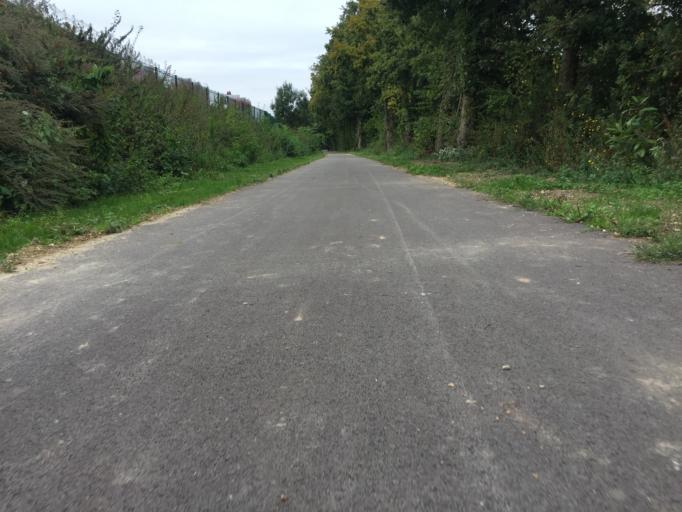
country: FR
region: Picardie
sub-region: Departement de l'Oise
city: Saint-Paul
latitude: 49.3994
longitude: 2.0130
